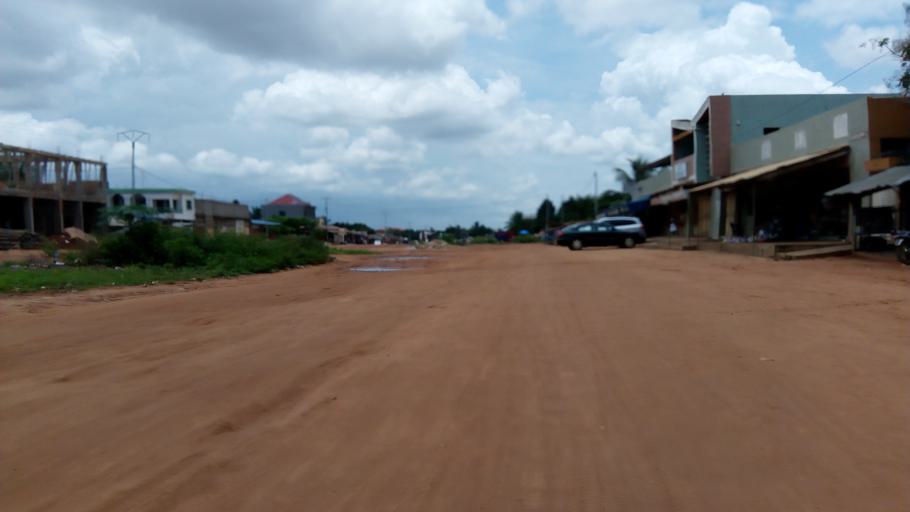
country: TG
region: Maritime
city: Lome
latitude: 6.2279
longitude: 1.1556
